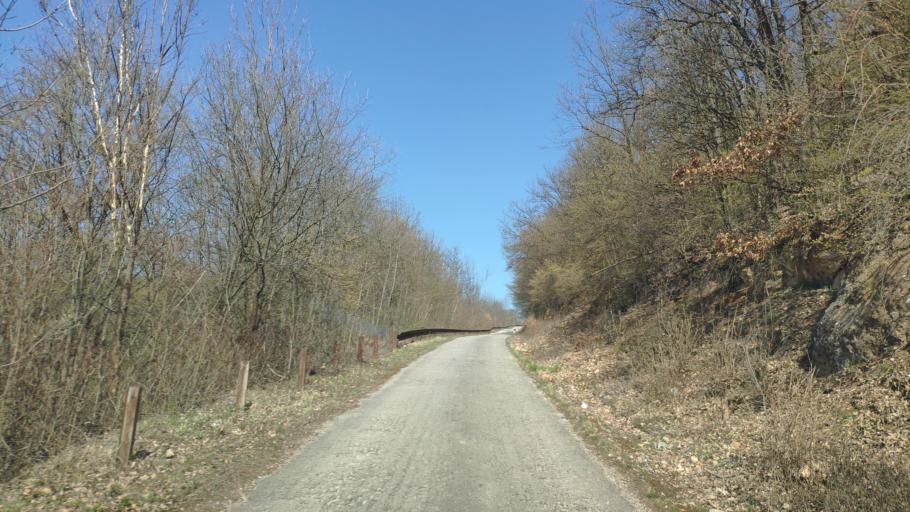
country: SK
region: Kosicky
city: Roznava
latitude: 48.5620
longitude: 20.4038
